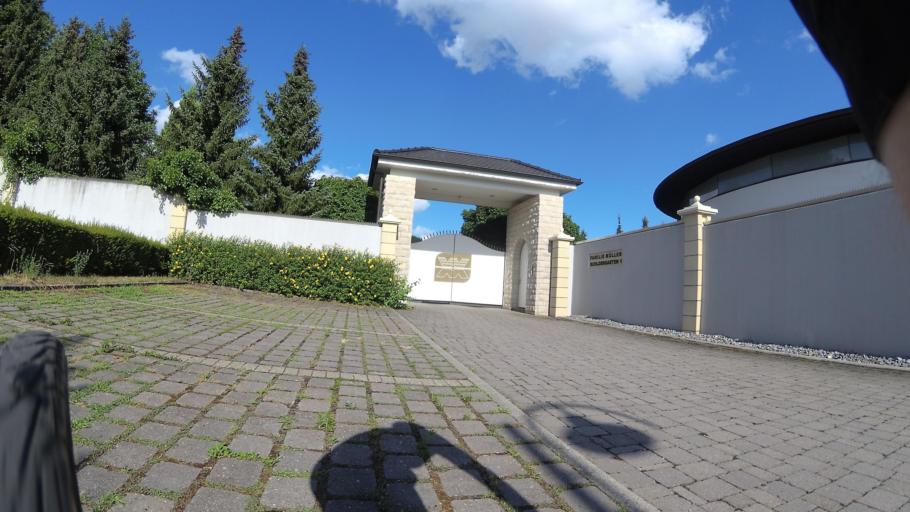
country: DE
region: Baden-Wuerttemberg
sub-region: Regierungsbezirk Stuttgart
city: Neuenstadt am Kocher
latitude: 49.2440
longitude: 9.3358
